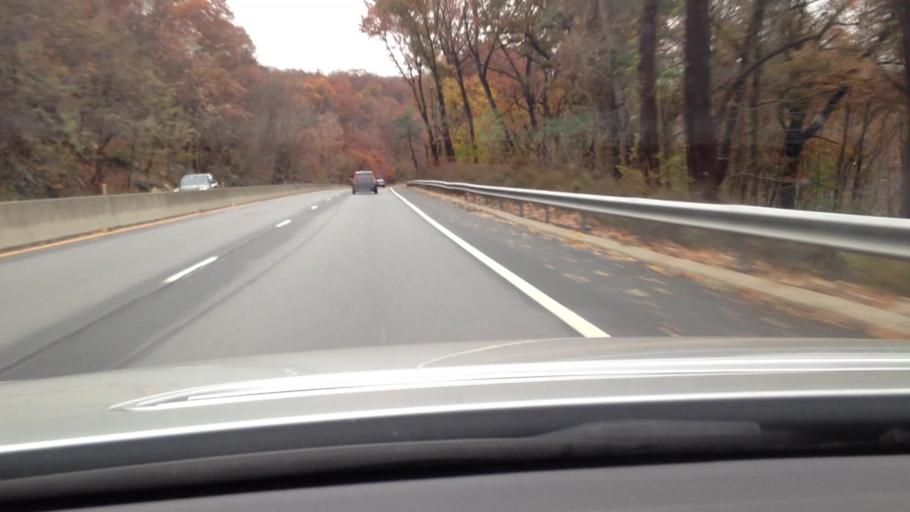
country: US
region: New York
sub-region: Westchester County
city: Elmsford
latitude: 41.0734
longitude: -73.8333
